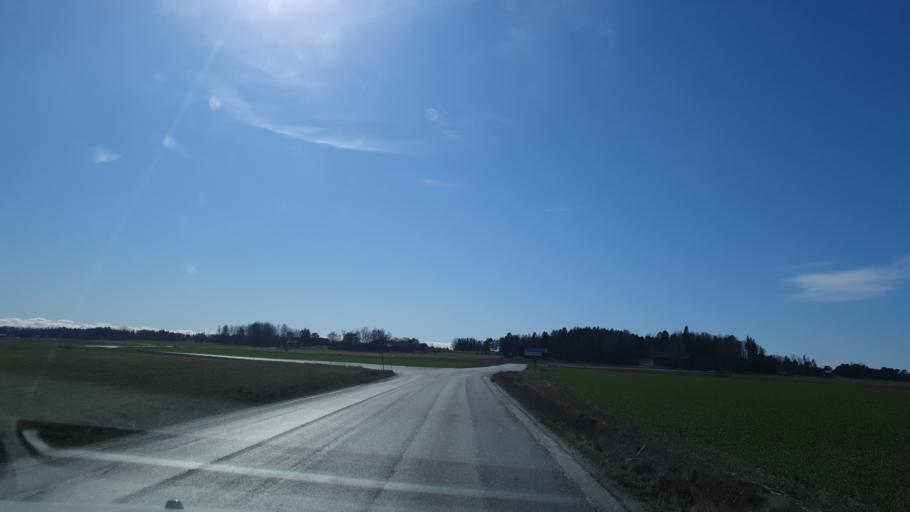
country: SE
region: Uppsala
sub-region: Enkopings Kommun
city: Grillby
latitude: 59.6033
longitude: 17.2729
